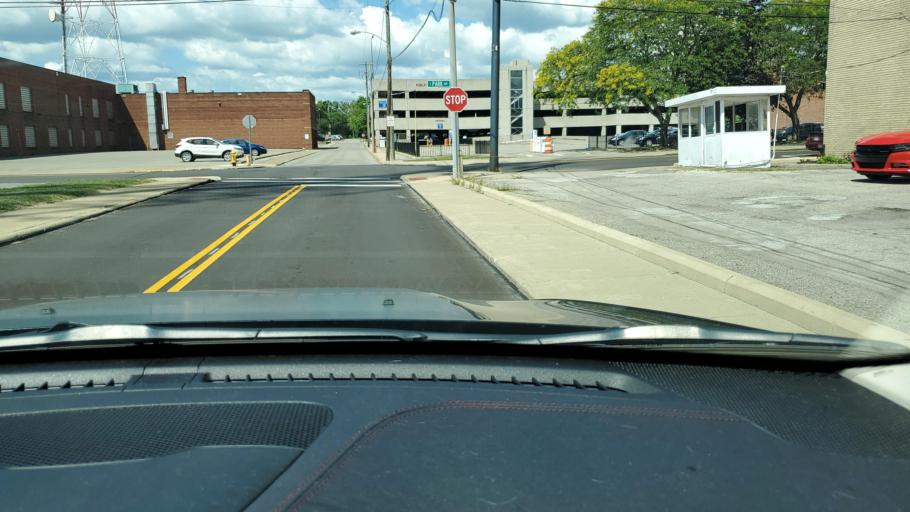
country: US
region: Ohio
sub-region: Trumbull County
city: Warren
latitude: 41.2349
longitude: -80.8175
